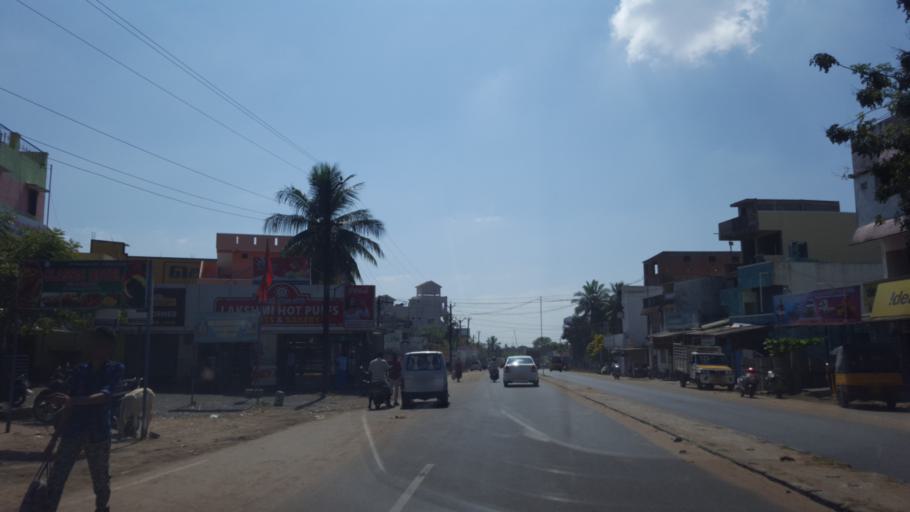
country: IN
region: Tamil Nadu
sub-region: Kancheepuram
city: Karumbakkam
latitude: 12.7204
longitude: 80.1872
